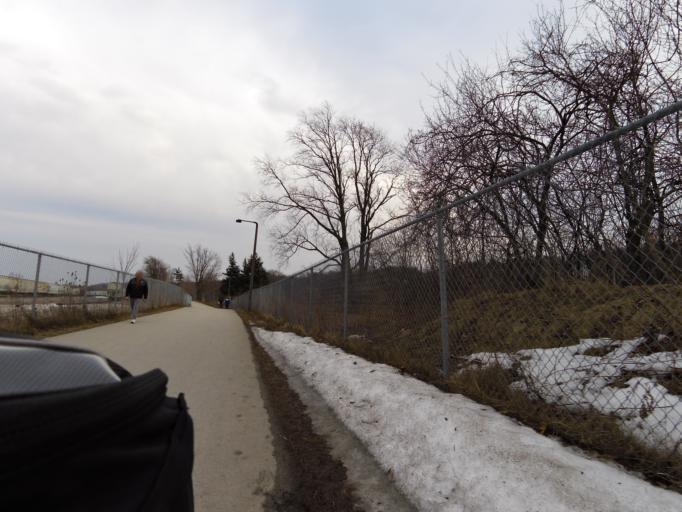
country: CA
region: Ontario
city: Hamilton
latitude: 43.2525
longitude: -79.9131
